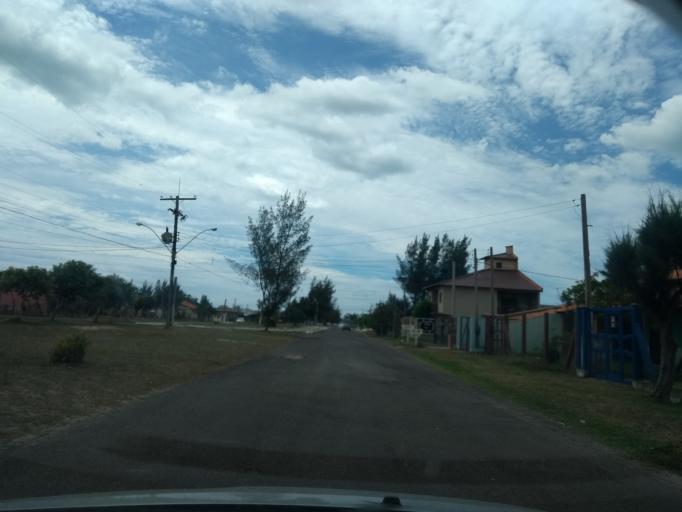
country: BR
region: Rio Grande do Sul
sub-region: Tramandai
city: Tramandai
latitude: -30.0618
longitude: -50.1648
